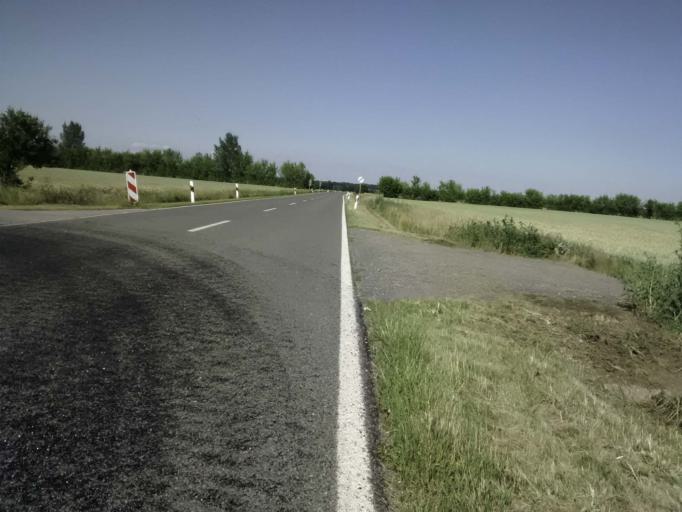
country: DE
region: Saxony-Anhalt
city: Gross Rosenburg
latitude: 51.9157
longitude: 11.9234
